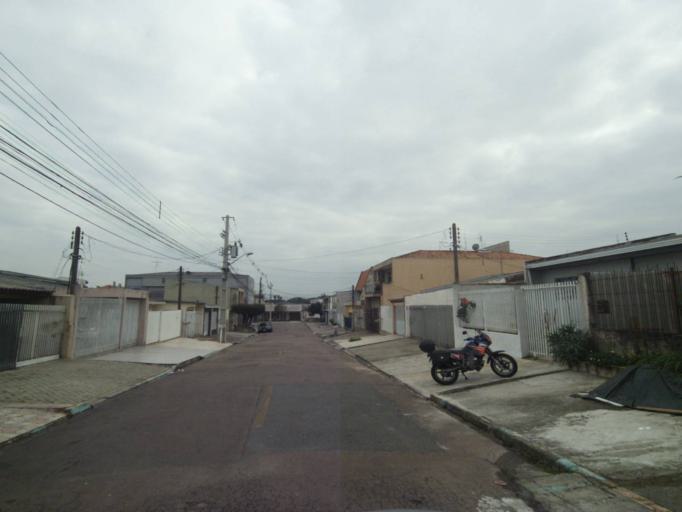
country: BR
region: Parana
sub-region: Curitiba
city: Curitiba
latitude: -25.5144
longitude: -49.3244
